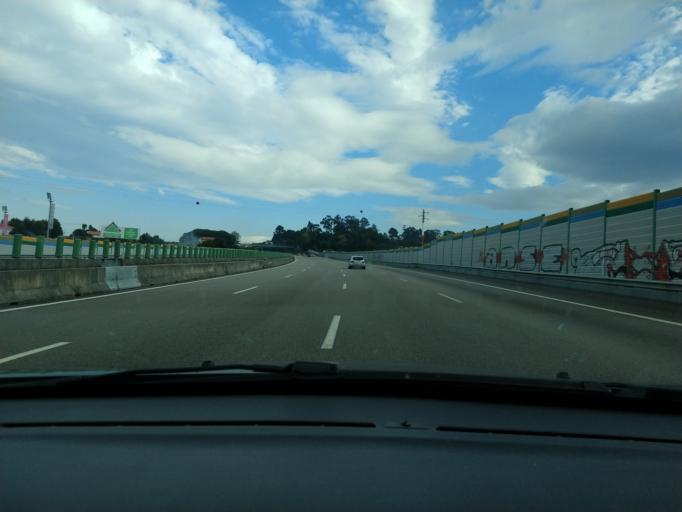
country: PT
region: Porto
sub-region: Vila Nova de Gaia
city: Grijo
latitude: 41.0239
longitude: -8.5759
